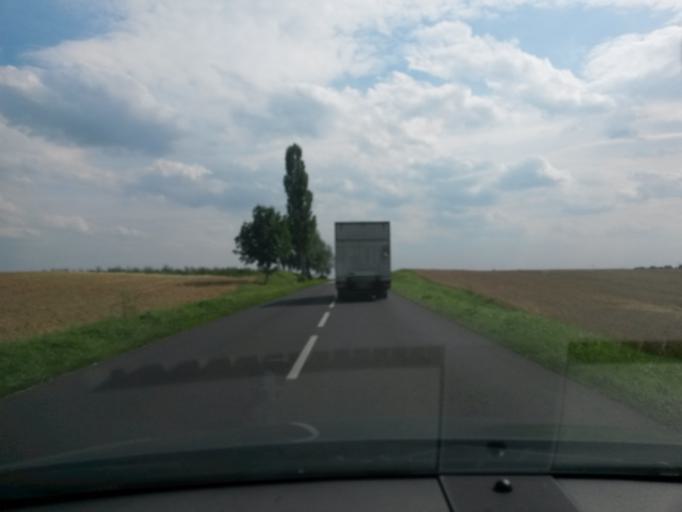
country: PL
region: Greater Poland Voivodeship
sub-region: Powiat poznanski
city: Kleszczewo
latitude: 52.2983
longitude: 17.1228
